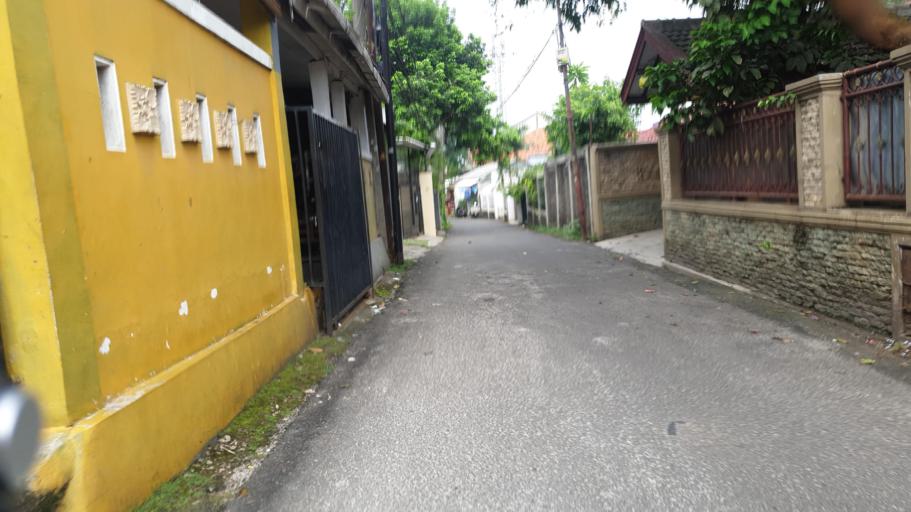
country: ID
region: West Java
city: Pamulang
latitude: -6.3032
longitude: 106.7890
